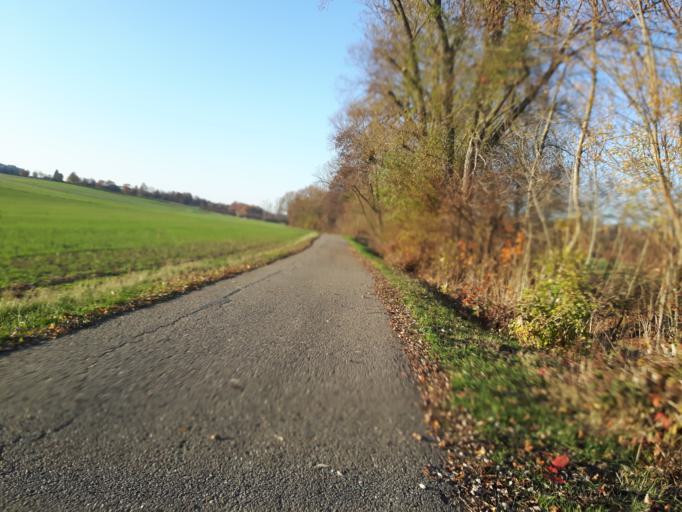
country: DE
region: Baden-Wuerttemberg
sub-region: Regierungsbezirk Stuttgart
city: Erlenbach
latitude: 49.1824
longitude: 9.2493
